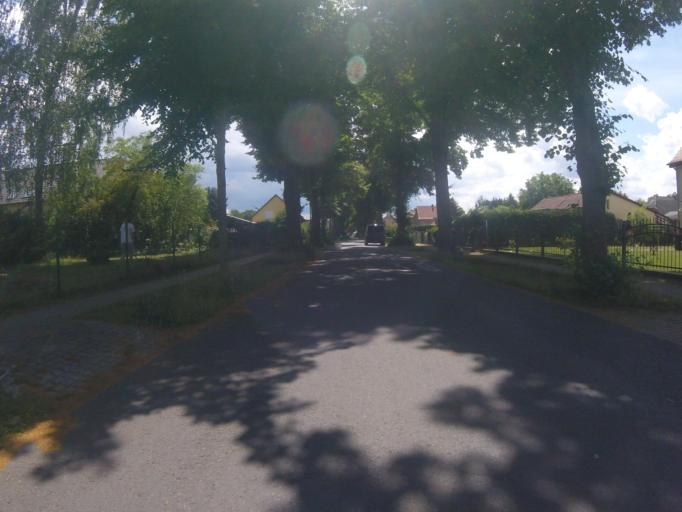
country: DE
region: Brandenburg
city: Konigs Wusterhausen
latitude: 52.2773
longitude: 13.6411
